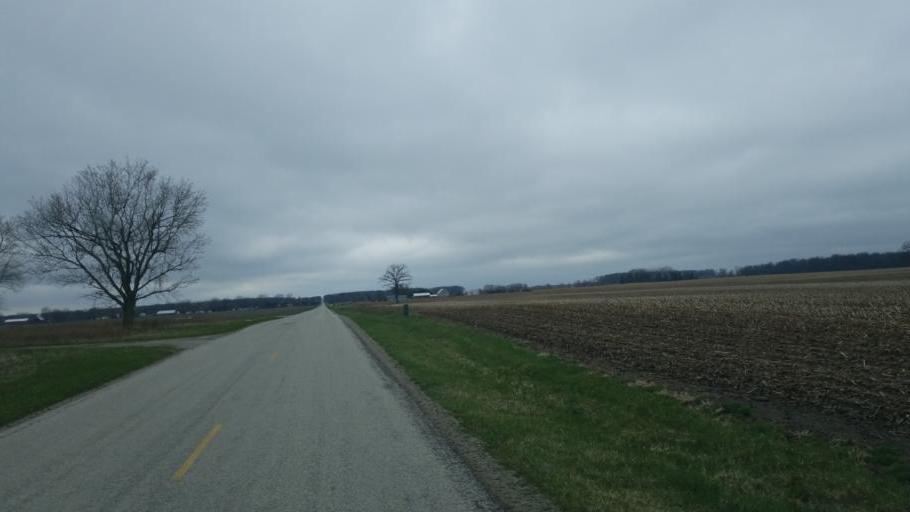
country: US
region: Ohio
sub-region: Marion County
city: Marion
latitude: 40.6737
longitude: -83.1292
